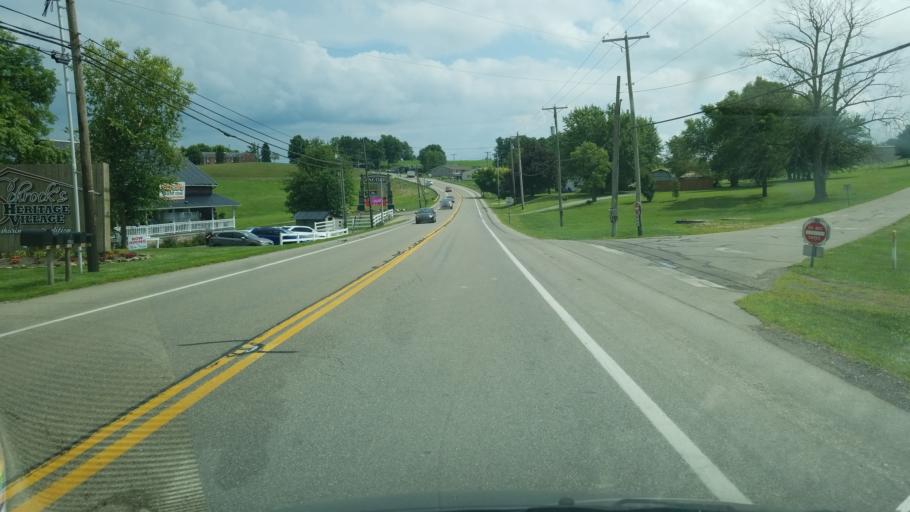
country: US
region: Ohio
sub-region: Holmes County
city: Millersburg
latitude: 40.5505
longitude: -81.7802
